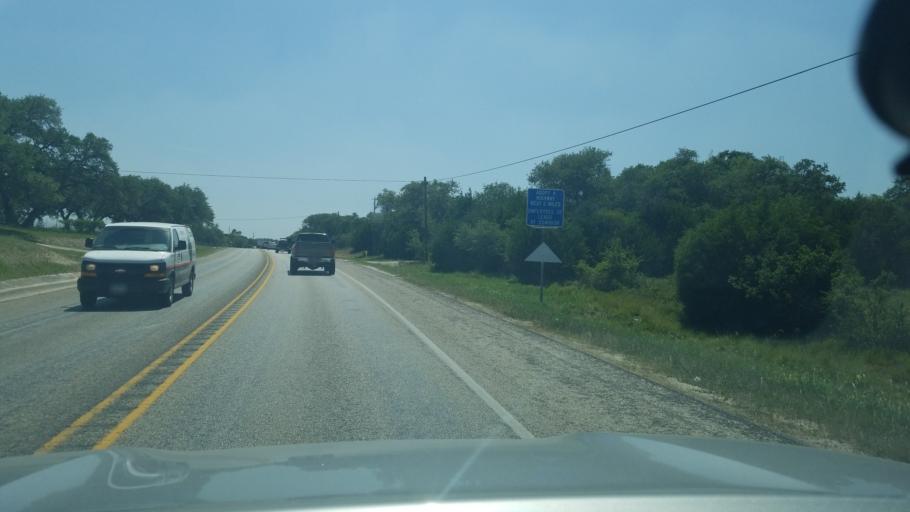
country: US
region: Texas
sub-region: Kendall County
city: Boerne
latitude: 29.7920
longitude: -98.6791
